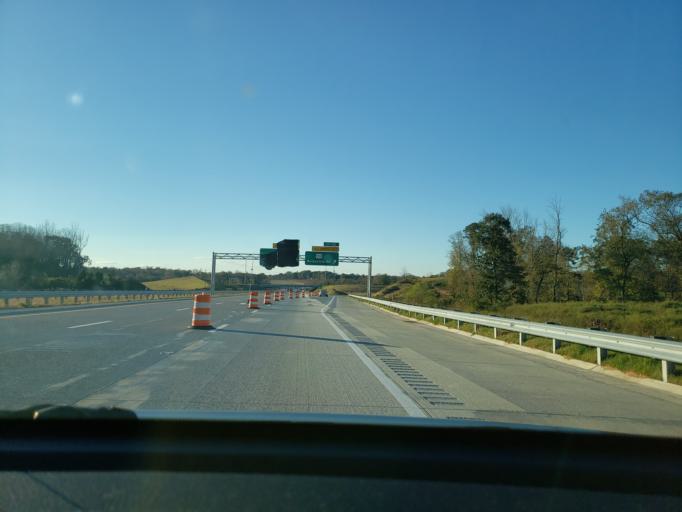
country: US
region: North Carolina
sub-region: Forsyth County
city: Walkertown
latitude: 36.1427
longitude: -80.1495
